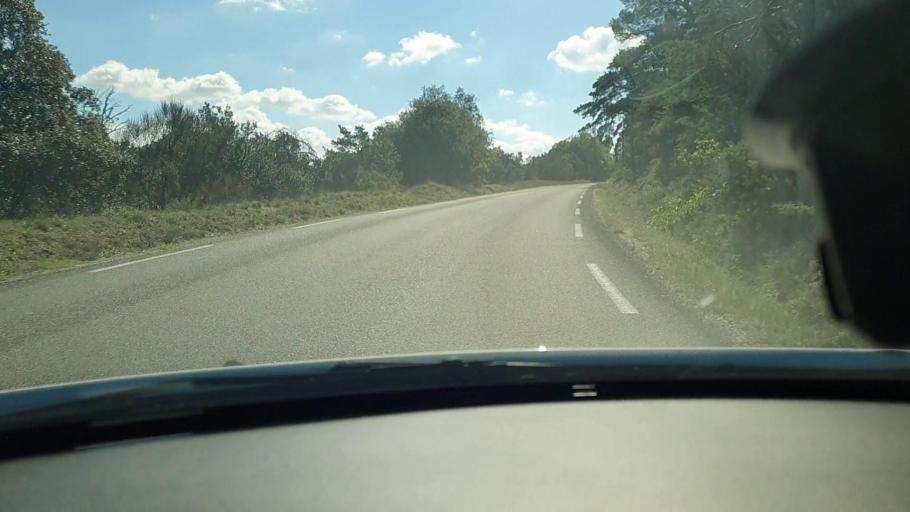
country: FR
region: Languedoc-Roussillon
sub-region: Departement du Gard
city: Goudargues
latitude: 44.1732
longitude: 4.4881
